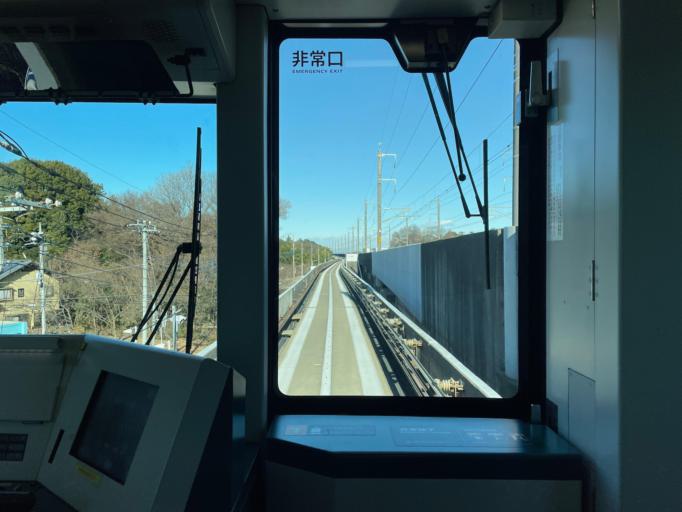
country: JP
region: Saitama
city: Ageoshimo
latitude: 35.9865
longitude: 139.6238
